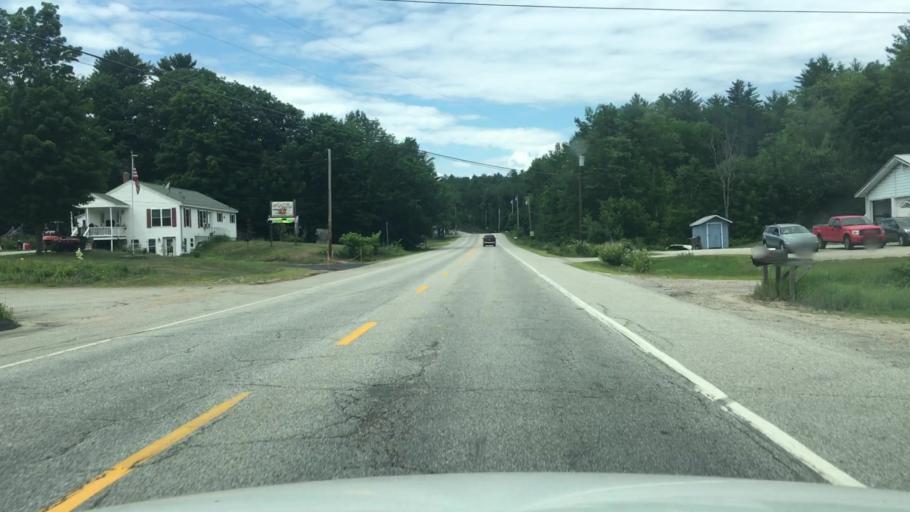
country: US
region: Maine
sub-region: Oxford County
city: West Paris
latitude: 44.3345
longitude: -70.5560
